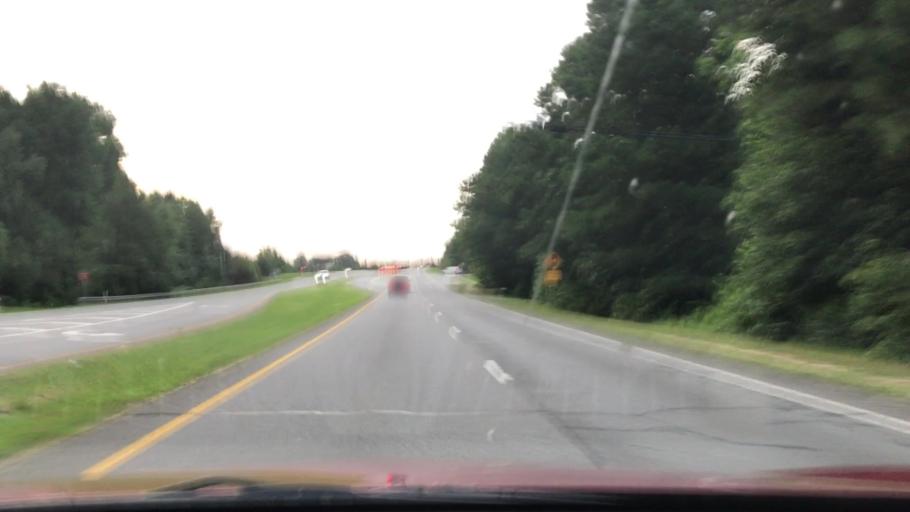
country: US
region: Georgia
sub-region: Gwinnett County
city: Lawrenceville
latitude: 34.0024
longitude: -83.9889
